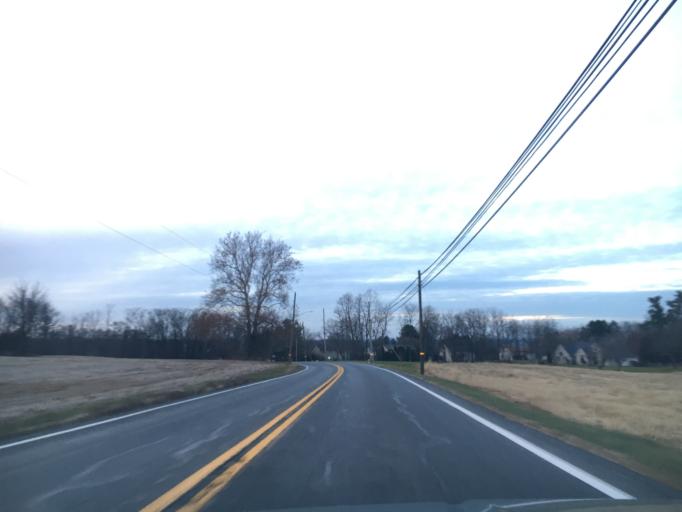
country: US
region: Pennsylvania
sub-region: Lehigh County
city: Stiles
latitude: 40.6421
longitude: -75.5162
